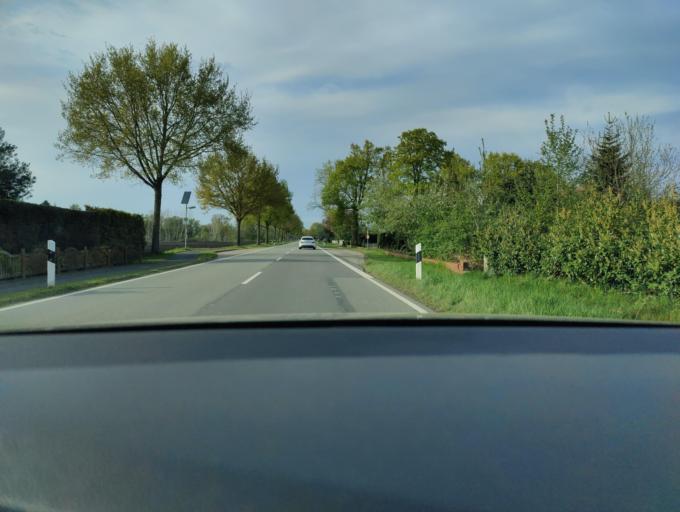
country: DE
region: Lower Saxony
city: Wietmarschen
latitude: 52.4866
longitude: 7.1177
